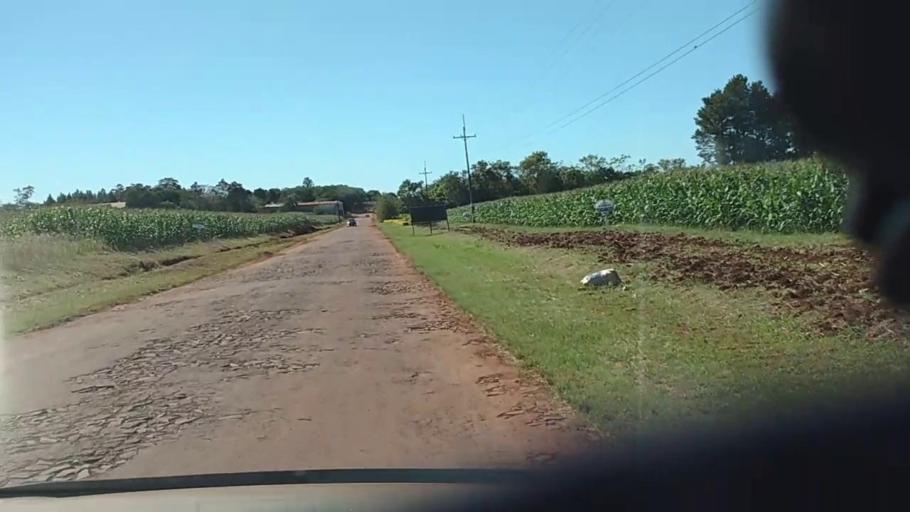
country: PY
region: Alto Parana
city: Naranjal
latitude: -25.9527
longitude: -55.1297
